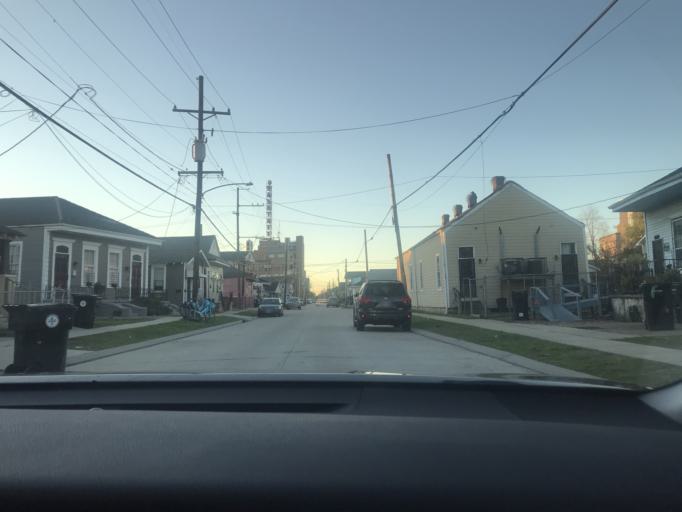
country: US
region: Louisiana
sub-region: Orleans Parish
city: New Orleans
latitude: 29.9587
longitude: -90.0872
